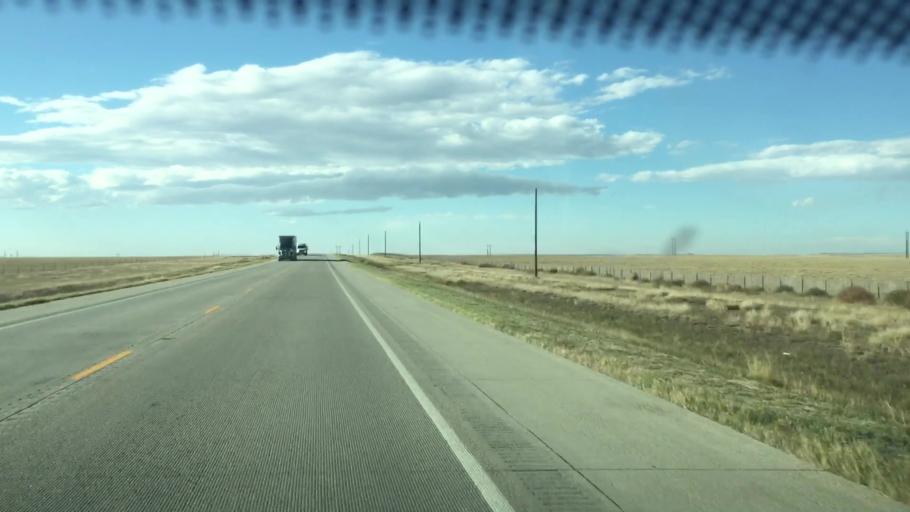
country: US
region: Colorado
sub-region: Lincoln County
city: Hugo
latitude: 39.0853
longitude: -103.3936
